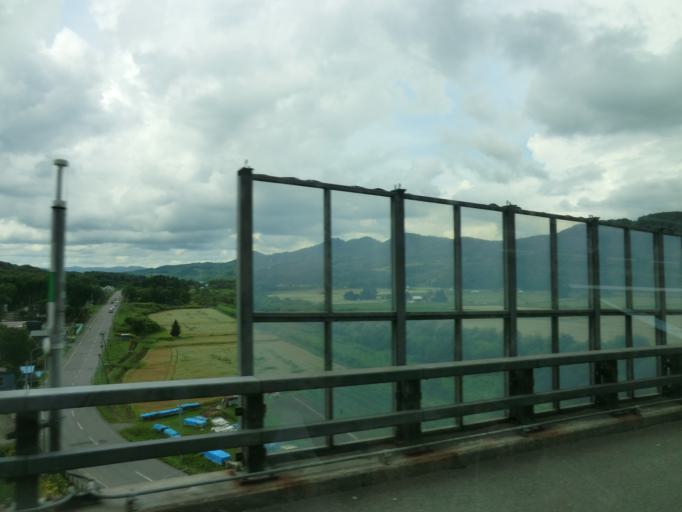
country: JP
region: Hokkaido
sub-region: Asahikawa-shi
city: Asahikawa
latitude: 43.7930
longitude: 142.2793
